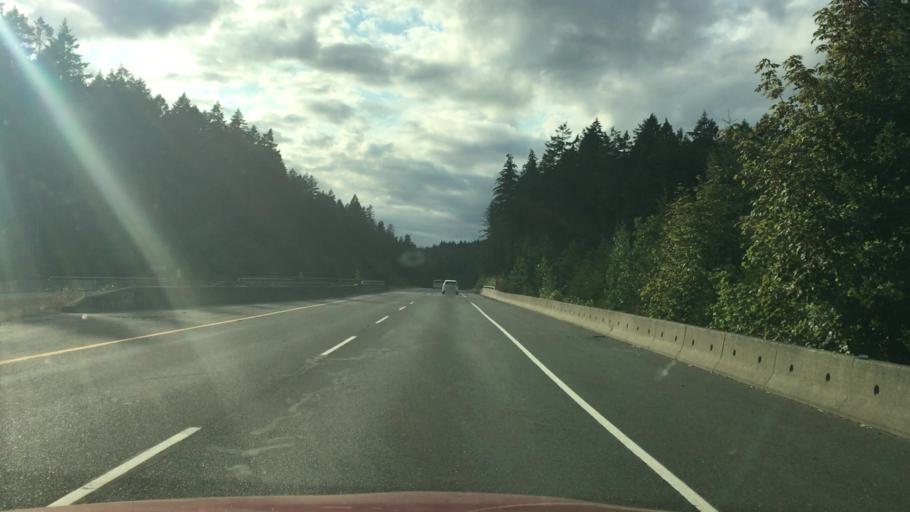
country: CA
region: British Columbia
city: Nanaimo
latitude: 49.1418
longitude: -123.9643
